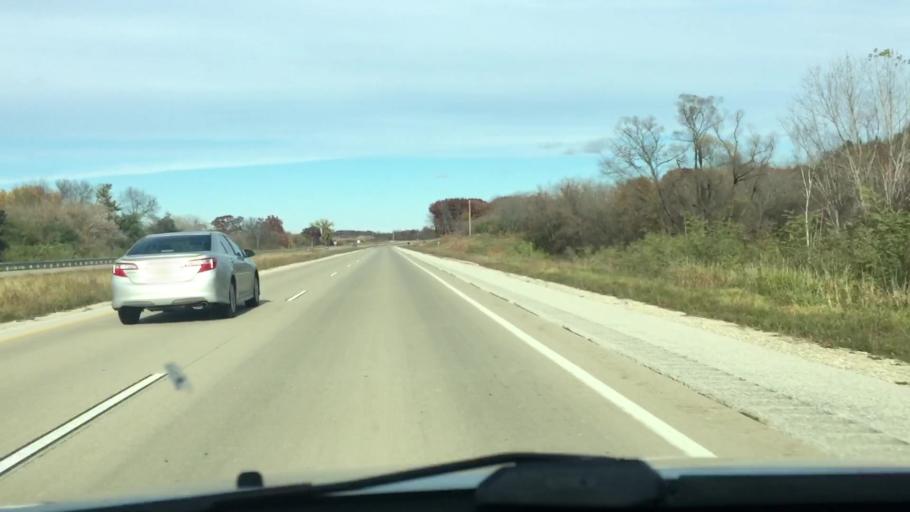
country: US
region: Wisconsin
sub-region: Kewaunee County
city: Luxemburg
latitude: 44.6987
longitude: -87.7112
